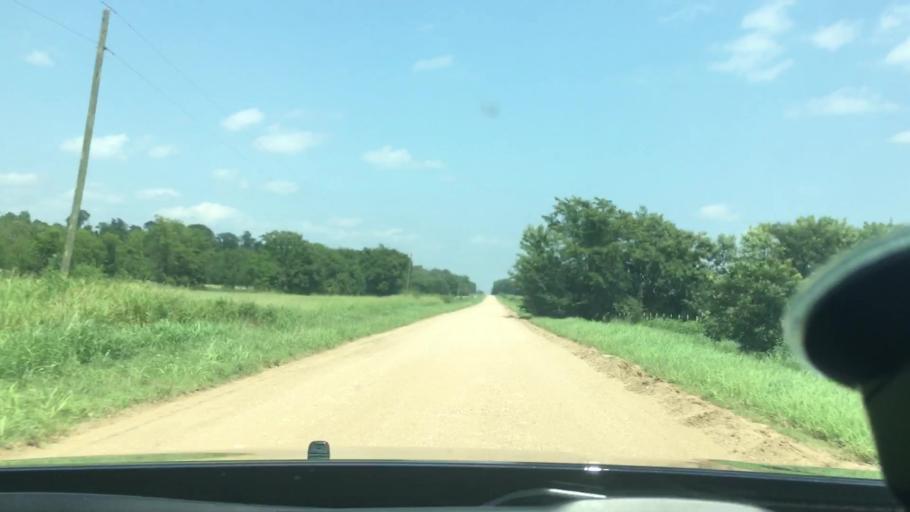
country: US
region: Oklahoma
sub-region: Johnston County
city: Tishomingo
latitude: 34.4223
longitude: -96.4742
